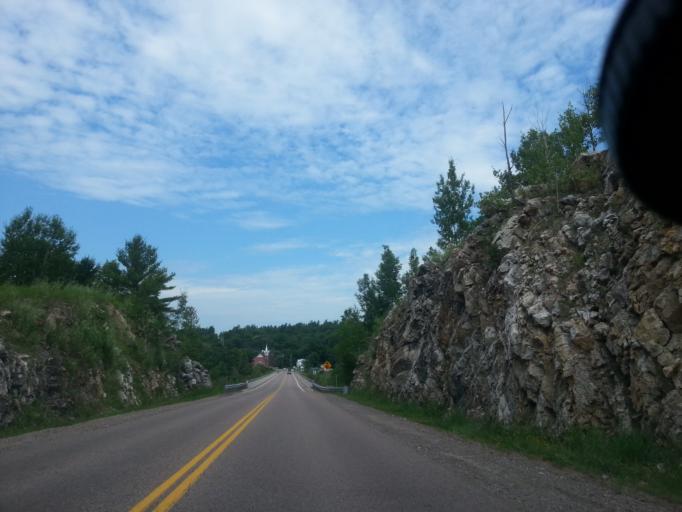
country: CA
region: Ontario
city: Renfrew
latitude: 45.3840
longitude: -76.5751
